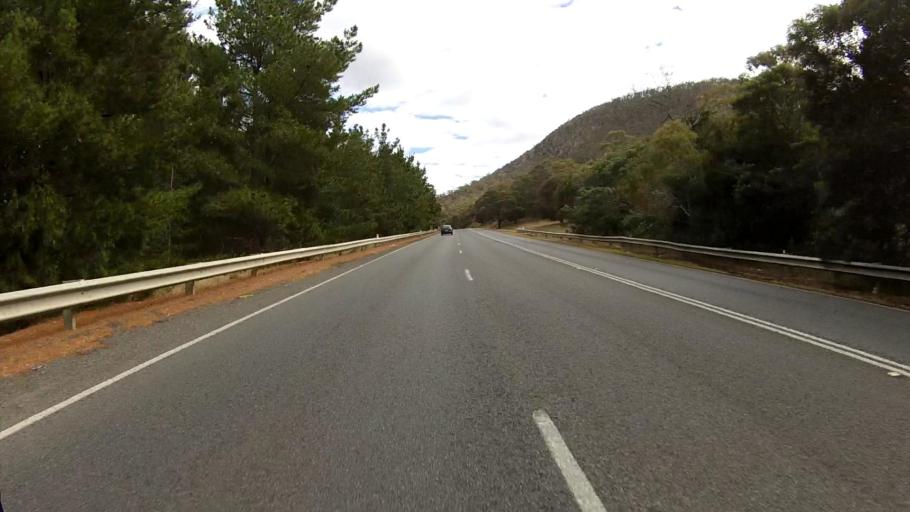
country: AU
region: Tasmania
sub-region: Glenorchy
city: Goodwood
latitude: -42.8097
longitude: 147.3019
